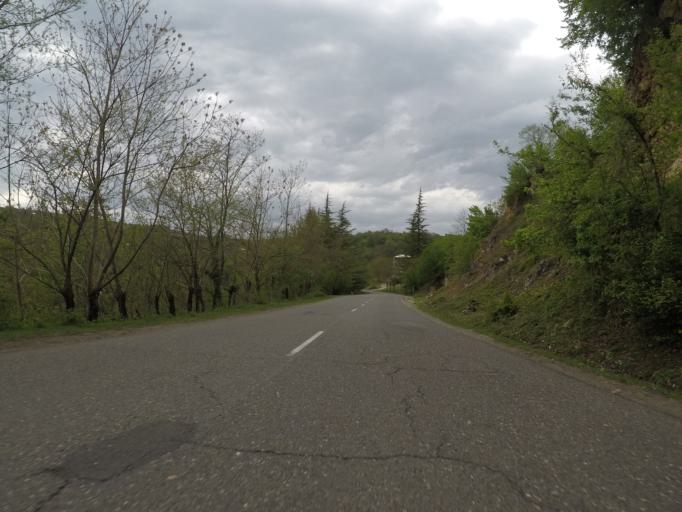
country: GE
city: Tqibuli
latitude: 42.2808
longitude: 43.2125
